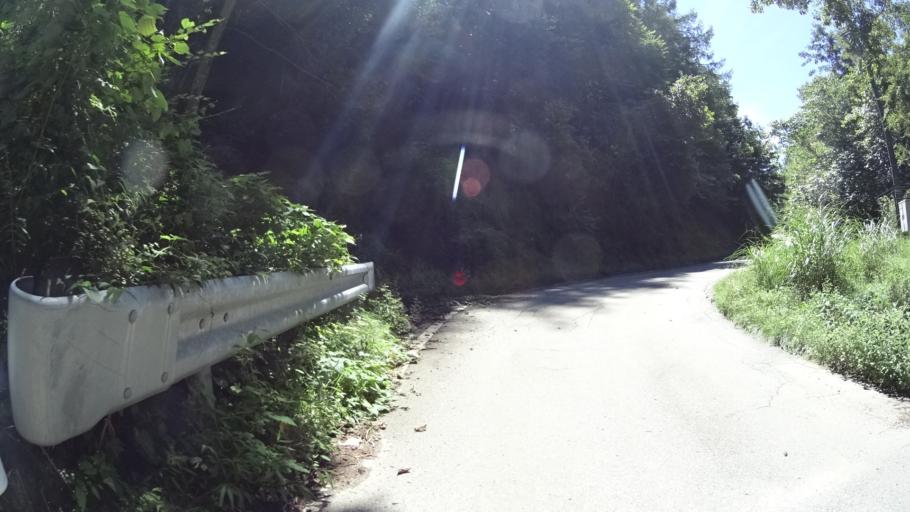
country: JP
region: Yamanashi
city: Enzan
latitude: 35.7434
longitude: 138.8289
